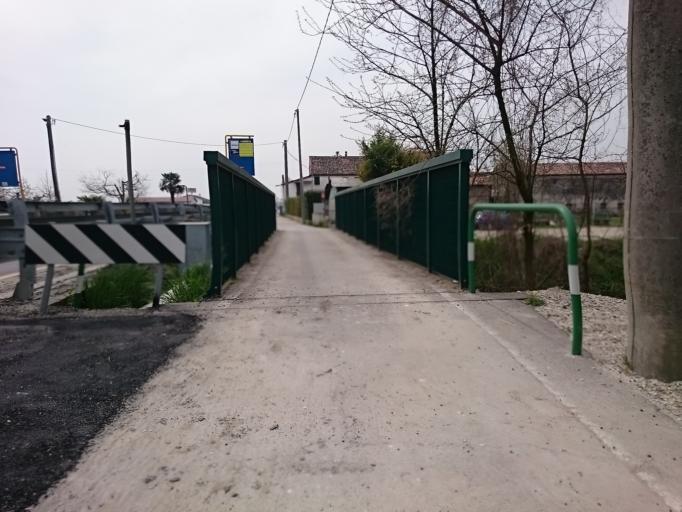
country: IT
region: Veneto
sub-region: Provincia di Padova
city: Bagnoli di Sopra
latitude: 45.1795
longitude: 11.8808
